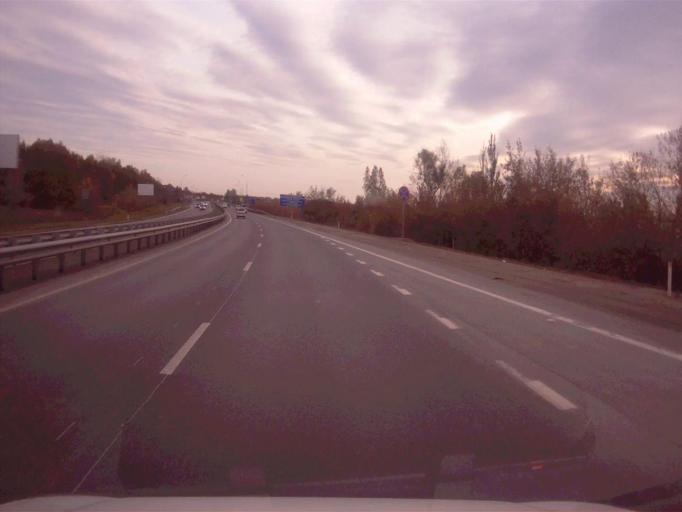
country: RU
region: Chelyabinsk
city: Novosineglazovskiy
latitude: 55.0353
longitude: 61.4422
